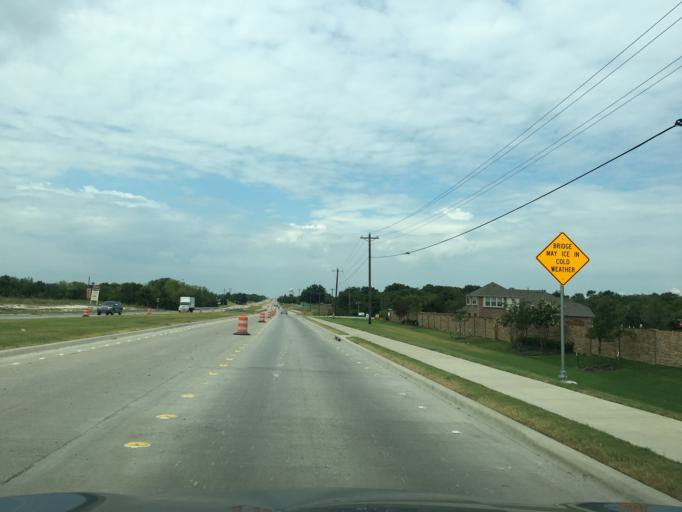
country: US
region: Texas
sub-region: Collin County
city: Melissa
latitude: 33.2913
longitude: -96.5481
